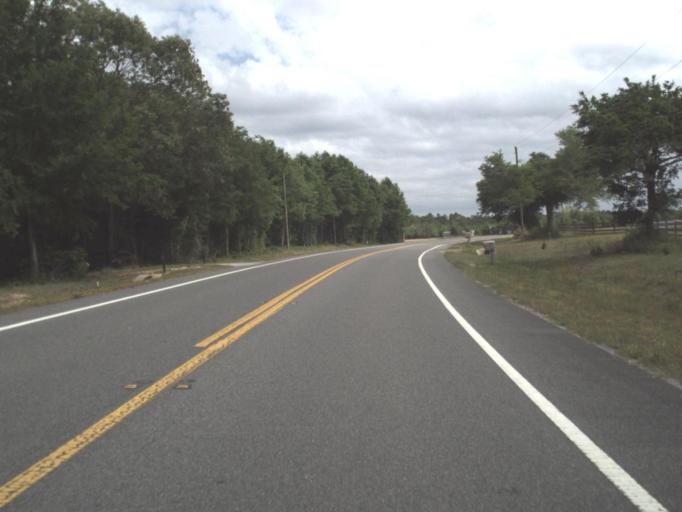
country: US
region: Florida
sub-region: Santa Rosa County
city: Point Baker
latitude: 30.7257
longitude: -87.0806
